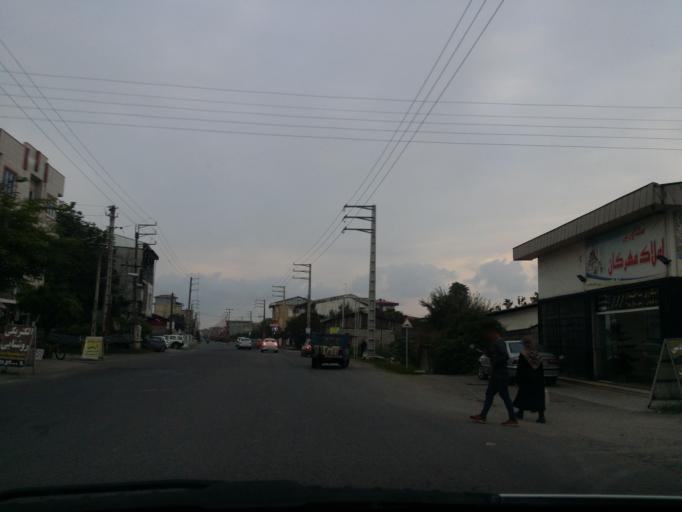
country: IR
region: Mazandaran
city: `Abbasabad
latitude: 36.7129
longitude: 51.1016
